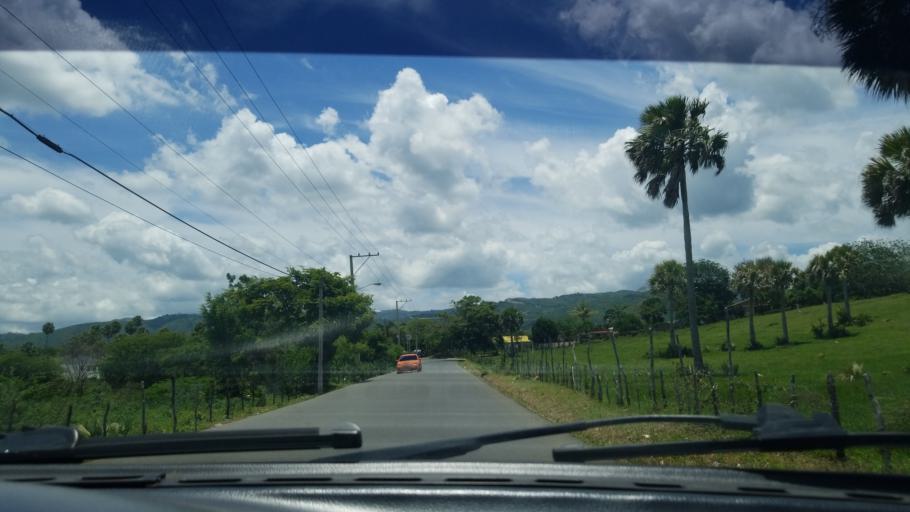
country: DO
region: Santiago
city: Santiago de los Caballeros
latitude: 19.4887
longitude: -70.6778
